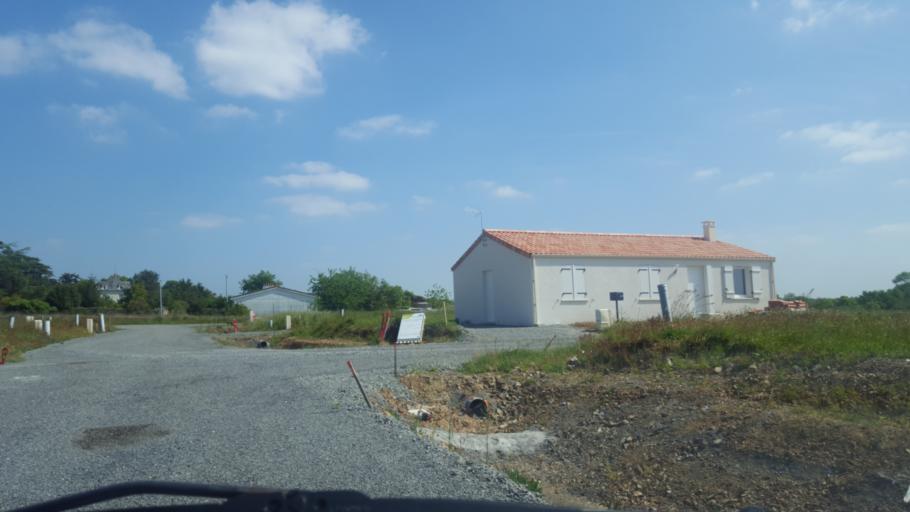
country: FR
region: Pays de la Loire
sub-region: Departement de la Loire-Atlantique
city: La Limouziniere
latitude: 46.9611
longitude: -1.5775
